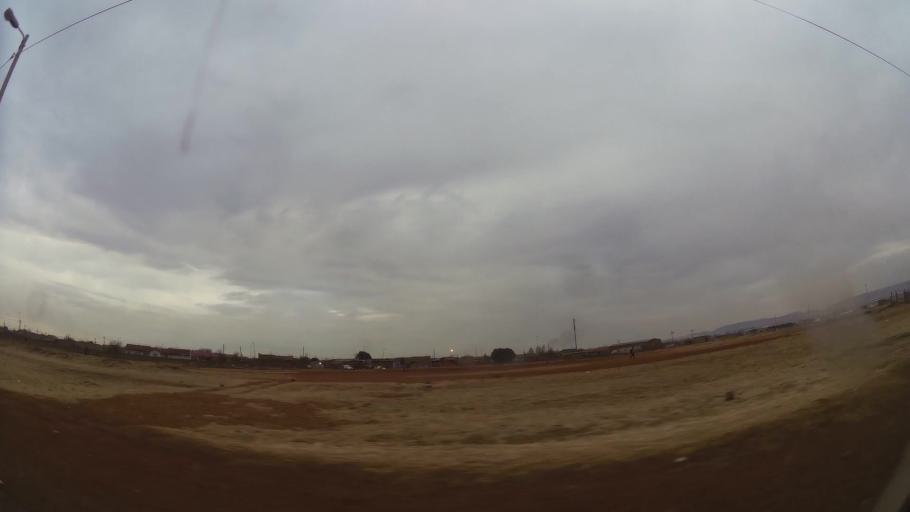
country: ZA
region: Gauteng
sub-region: Ekurhuleni Metropolitan Municipality
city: Germiston
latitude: -26.3838
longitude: 28.1836
